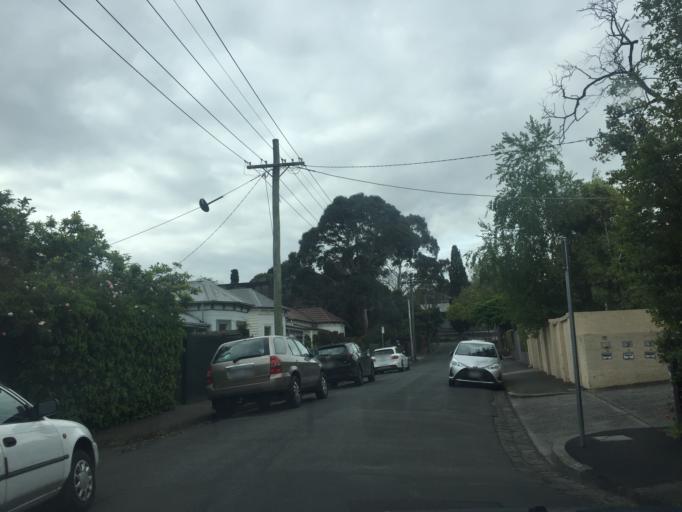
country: AU
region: Victoria
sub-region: Boroondara
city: Hawthorn East
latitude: -37.8213
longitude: 145.0500
